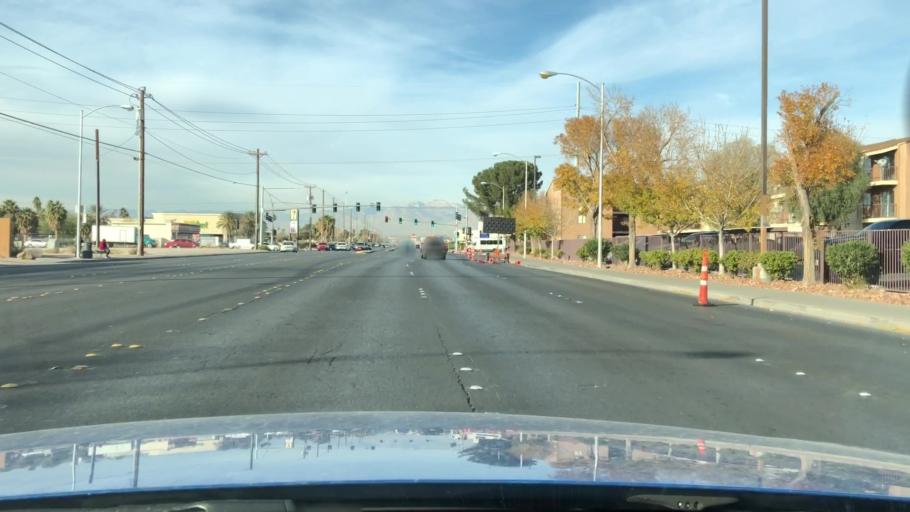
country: US
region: Nevada
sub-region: Clark County
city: North Las Vegas
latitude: 36.1958
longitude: -115.0967
